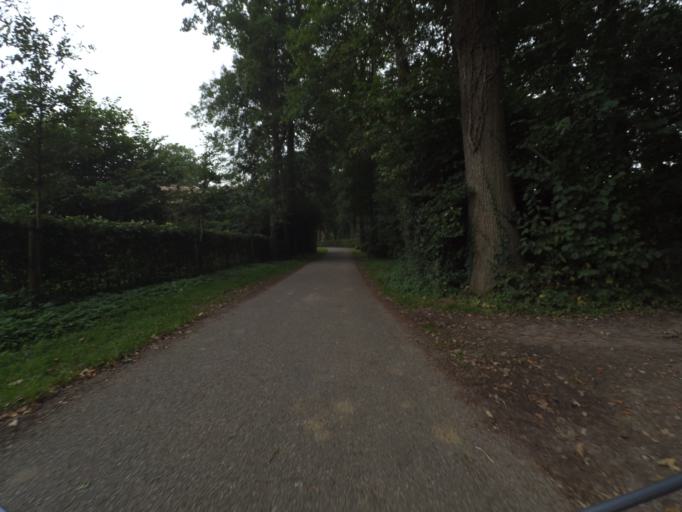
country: NL
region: Overijssel
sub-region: Gemeente Oldenzaal
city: Oldenzaal
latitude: 52.3097
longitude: 6.9643
